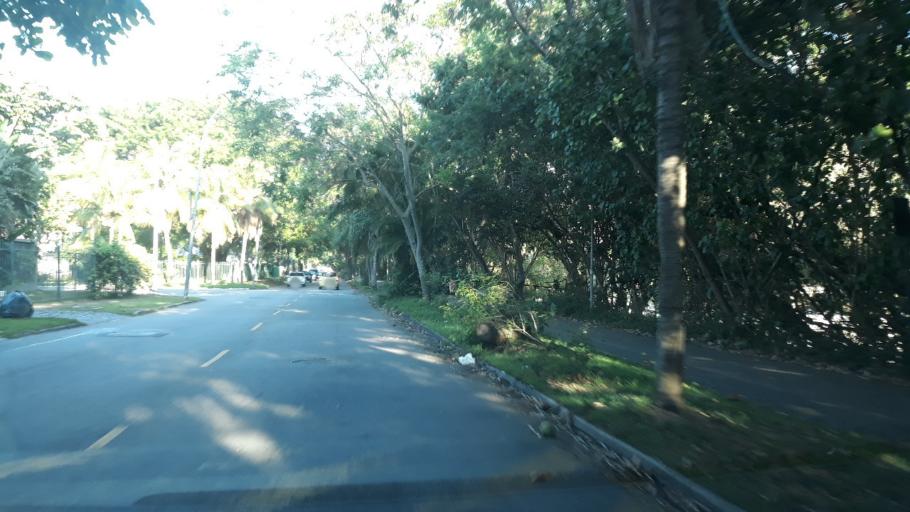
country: BR
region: Rio de Janeiro
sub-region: Rio De Janeiro
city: Rio de Janeiro
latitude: -23.0062
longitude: -43.3360
